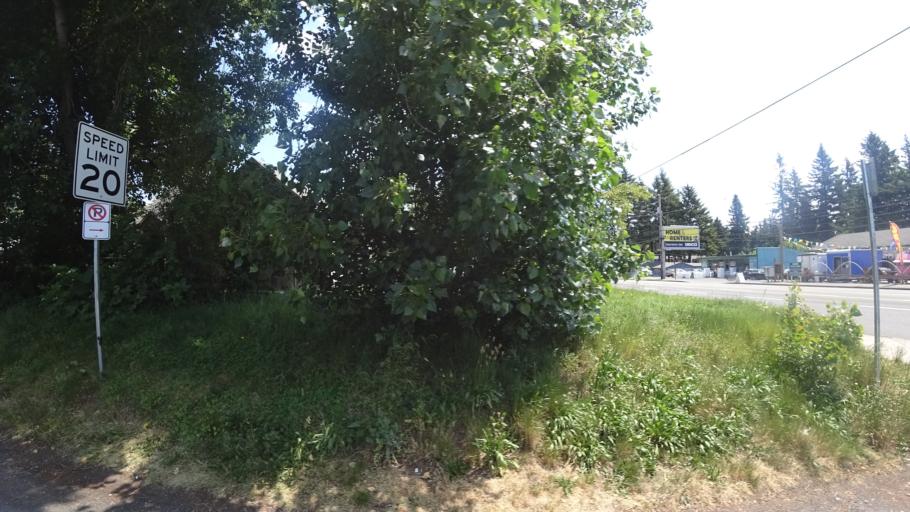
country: US
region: Oregon
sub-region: Multnomah County
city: Fairview
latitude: 45.5266
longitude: -122.5016
